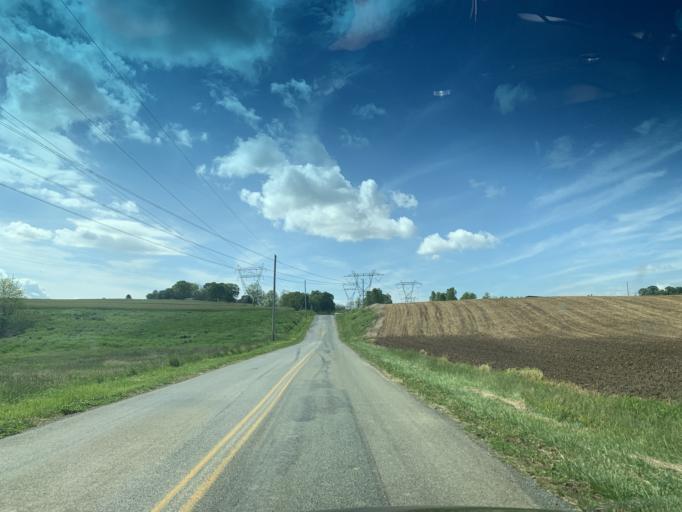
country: US
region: Maryland
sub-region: Cecil County
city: Rising Sun
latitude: 39.7272
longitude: -76.1873
